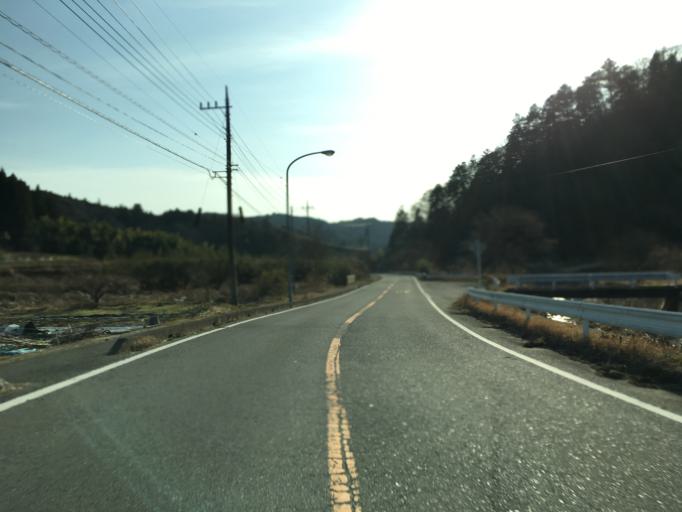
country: JP
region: Ibaraki
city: Daigo
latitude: 36.7204
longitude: 140.5069
